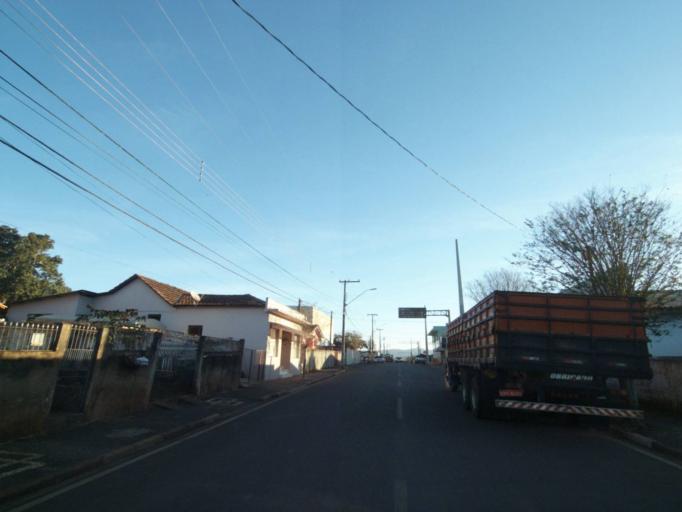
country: BR
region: Parana
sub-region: Tibagi
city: Tibagi
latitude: -24.5187
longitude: -50.4116
